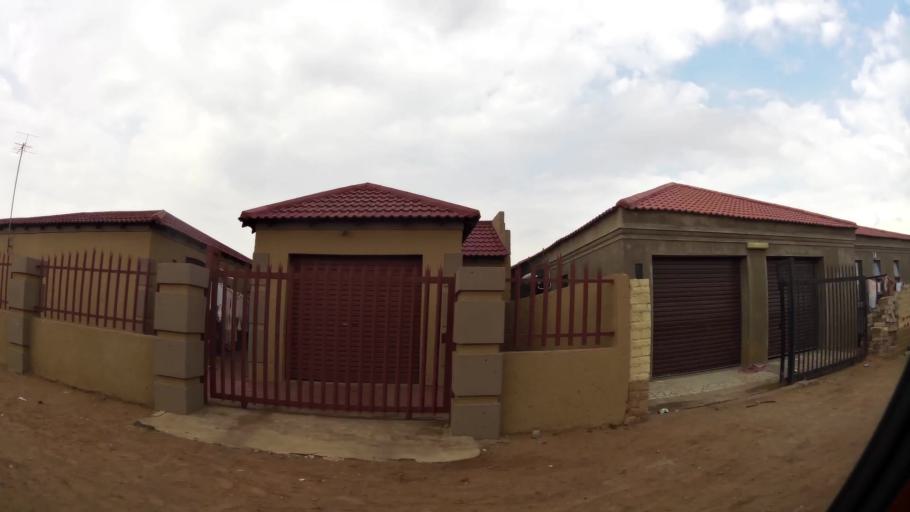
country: ZA
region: Gauteng
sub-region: Sedibeng District Municipality
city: Vanderbijlpark
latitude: -26.6649
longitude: 27.8531
